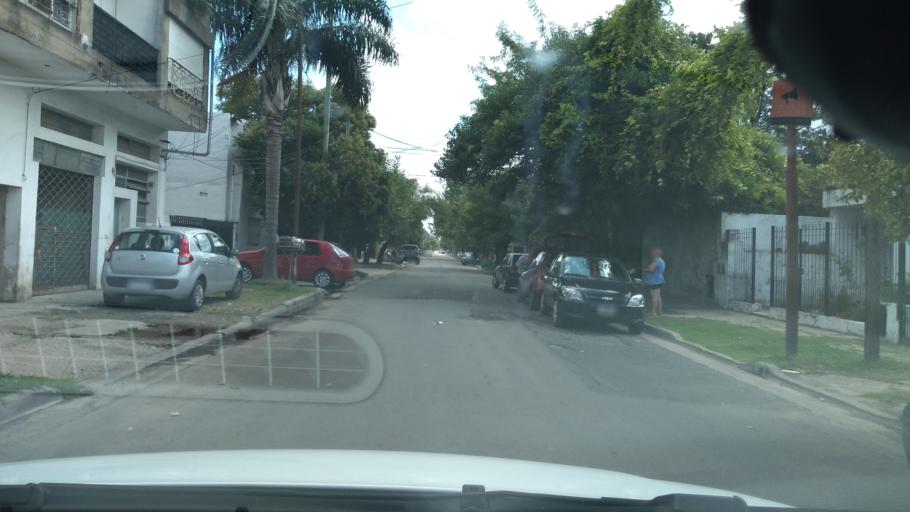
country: AR
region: Buenos Aires
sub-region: Partido de Moron
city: Moron
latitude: -34.6694
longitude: -58.6079
